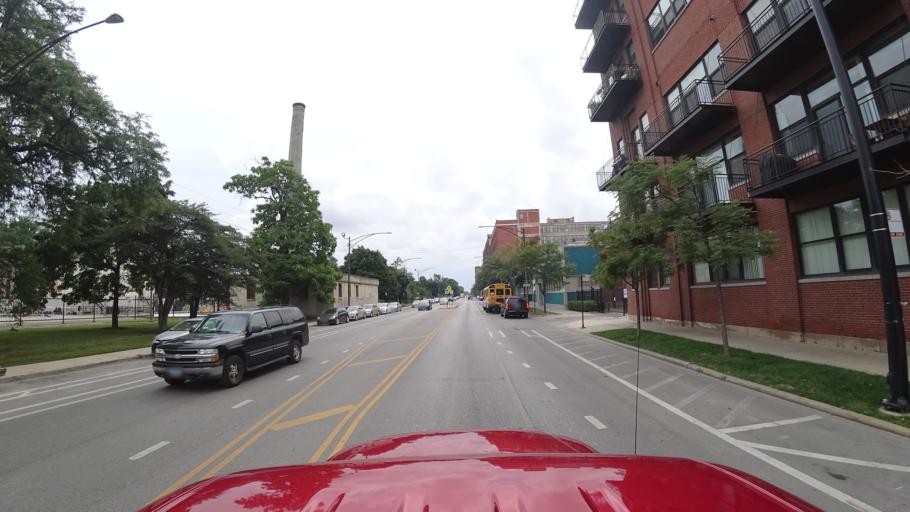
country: US
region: Illinois
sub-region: Cook County
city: Chicago
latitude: 41.8230
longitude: -87.6831
